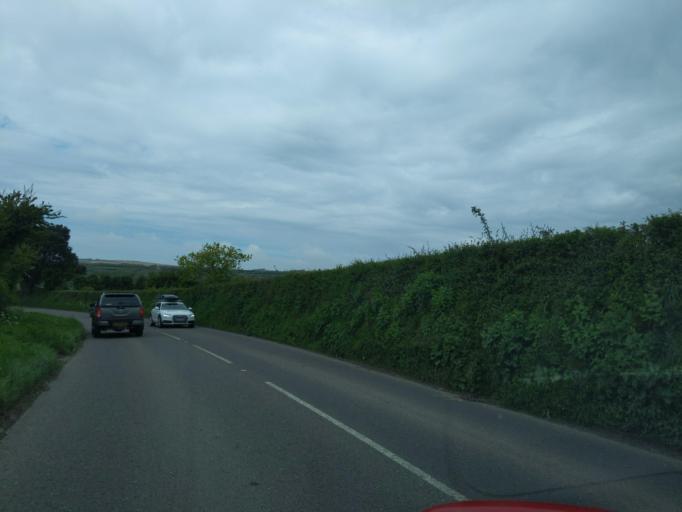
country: GB
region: England
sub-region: Cornwall
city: Wadebridge
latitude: 50.5315
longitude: -4.8365
